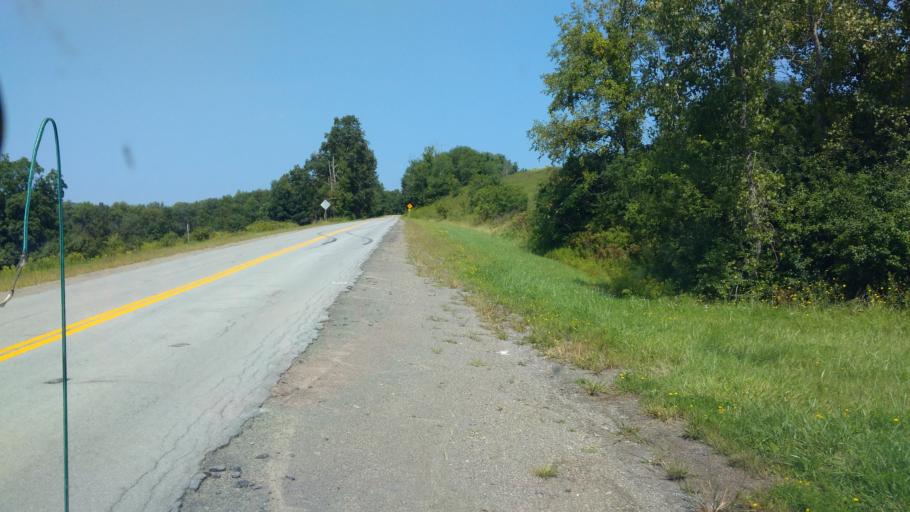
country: US
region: New York
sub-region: Allegany County
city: Belmont
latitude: 42.2711
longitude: -78.0516
